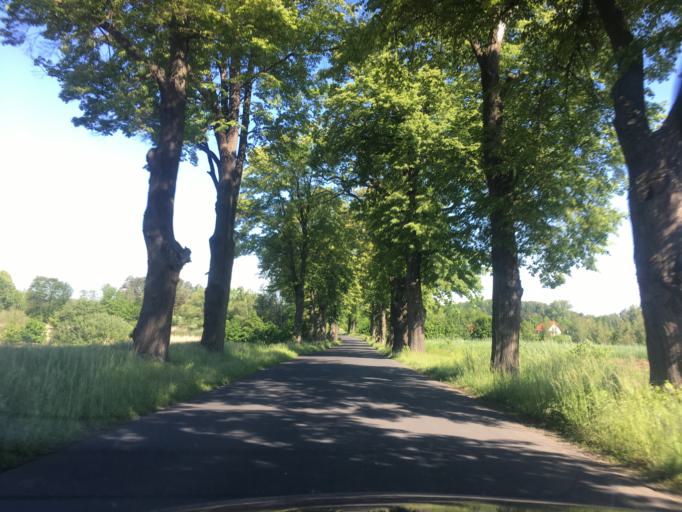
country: PL
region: Lower Silesian Voivodeship
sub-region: Powiat zgorzelecki
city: Sulikow
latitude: 51.1069
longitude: 15.0354
